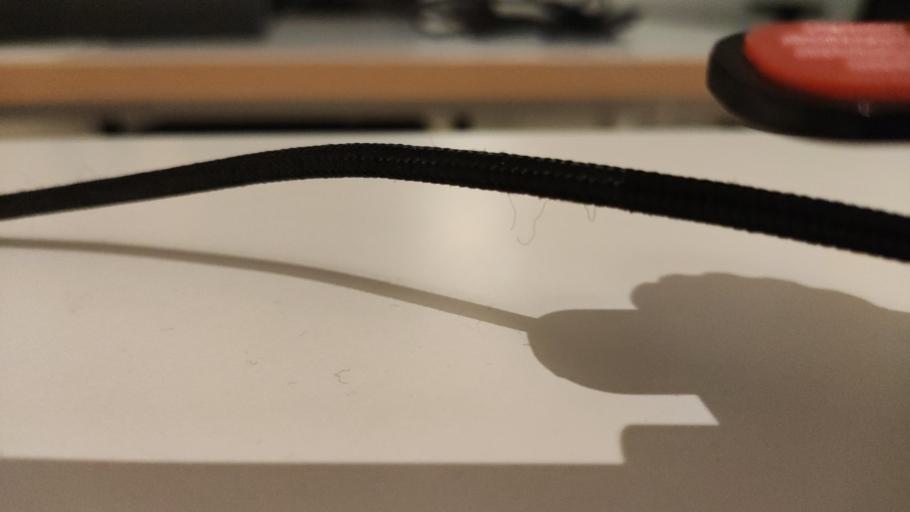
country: RU
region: Moskovskaya
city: Novoye
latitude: 55.6102
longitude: 38.9296
